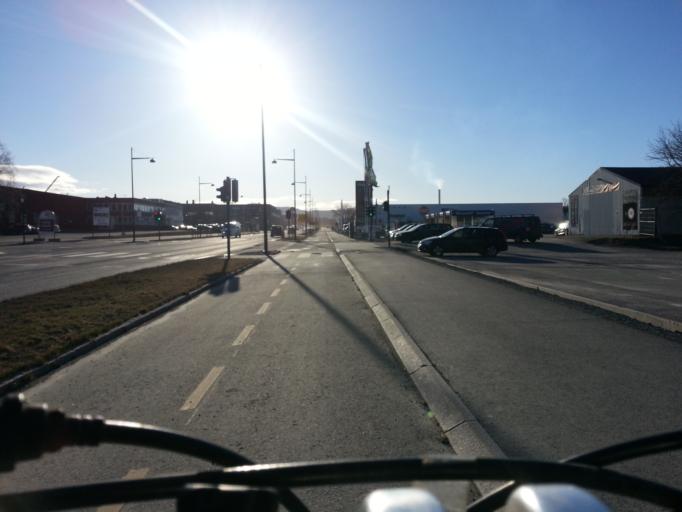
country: NO
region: Sor-Trondelag
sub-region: Trondheim
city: Trondheim
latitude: 63.4425
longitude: 10.4533
